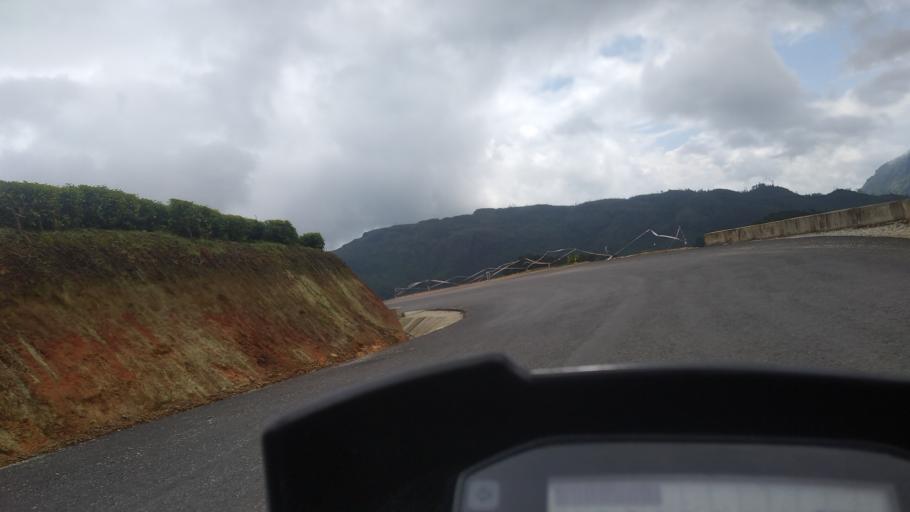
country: IN
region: Kerala
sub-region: Idukki
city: Munnar
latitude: 10.0771
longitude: 77.0873
